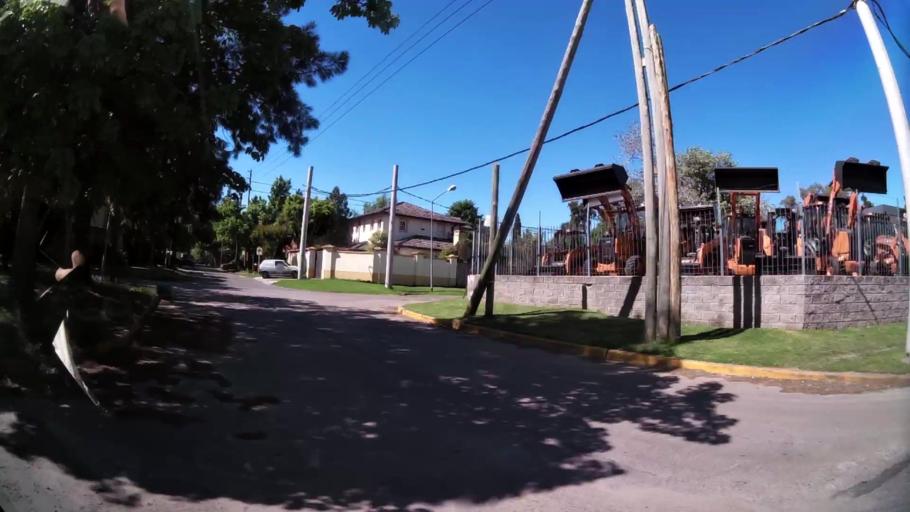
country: AR
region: Buenos Aires
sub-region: Partido de Tigre
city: Tigre
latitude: -34.4845
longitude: -58.6255
